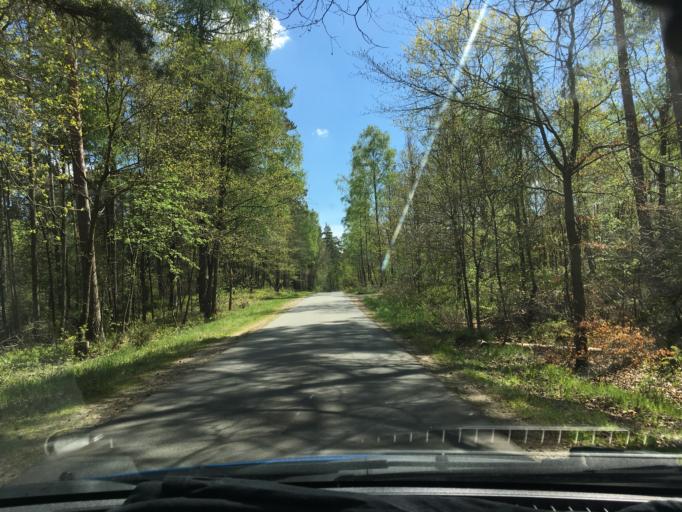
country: DE
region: Lower Saxony
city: Stoetze
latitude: 53.0999
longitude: 10.7827
